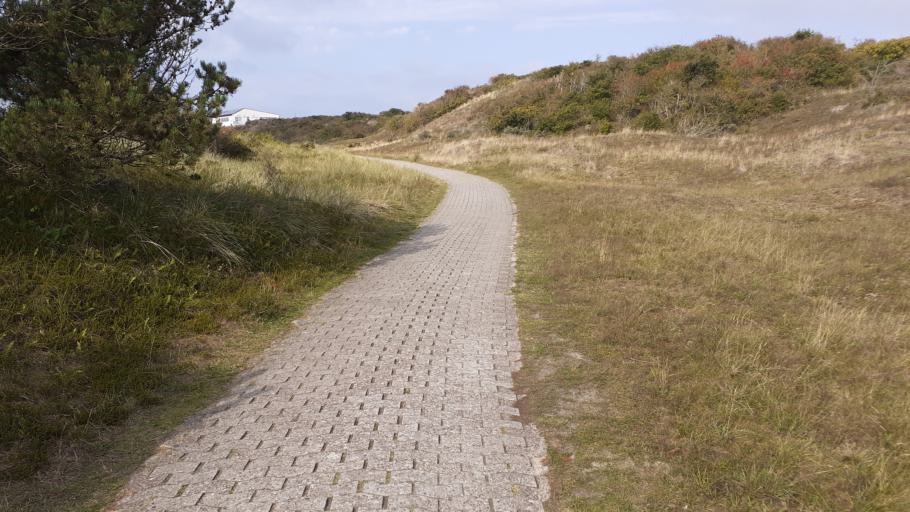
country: DE
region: Lower Saxony
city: Spiekeroog
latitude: 53.7779
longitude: 7.7006
